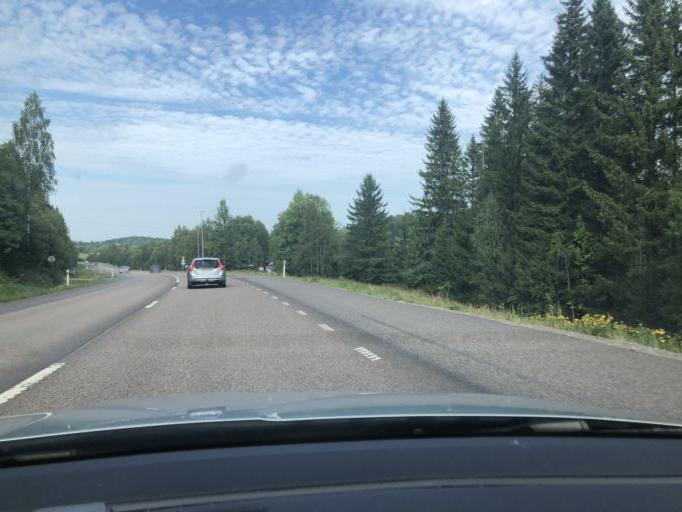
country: SE
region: Vaesternorrland
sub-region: Kramfors Kommun
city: Kramfors
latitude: 62.8959
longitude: 17.8492
